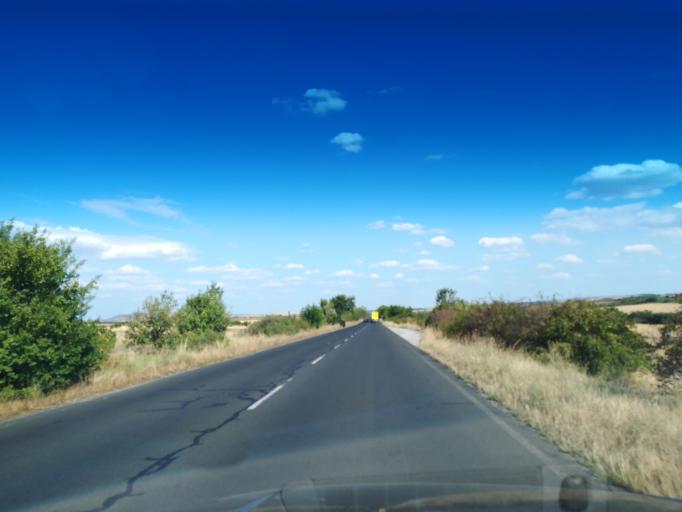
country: BG
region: Stara Zagora
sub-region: Obshtina Chirpan
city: Chirpan
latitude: 42.0573
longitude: 25.2914
